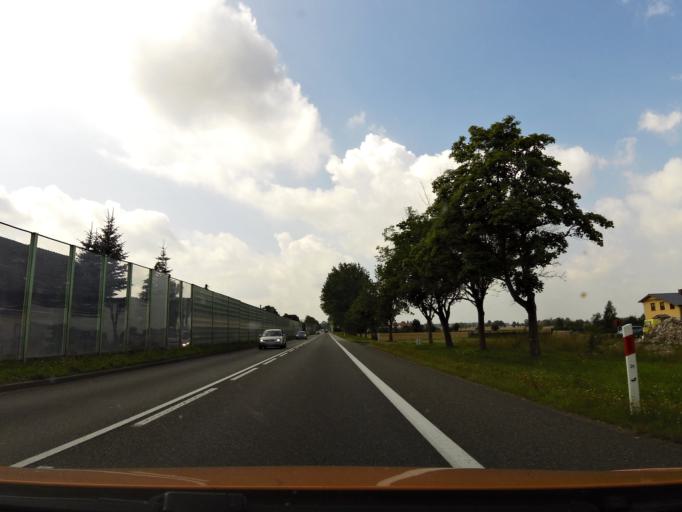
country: PL
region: West Pomeranian Voivodeship
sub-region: Powiat goleniowski
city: Nowogard
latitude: 53.6467
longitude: 15.0629
